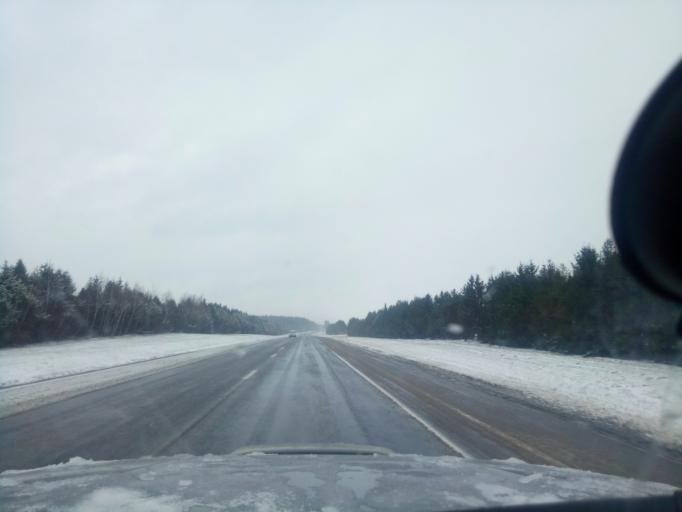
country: BY
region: Minsk
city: Haradzyeya
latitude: 53.2899
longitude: 26.5796
